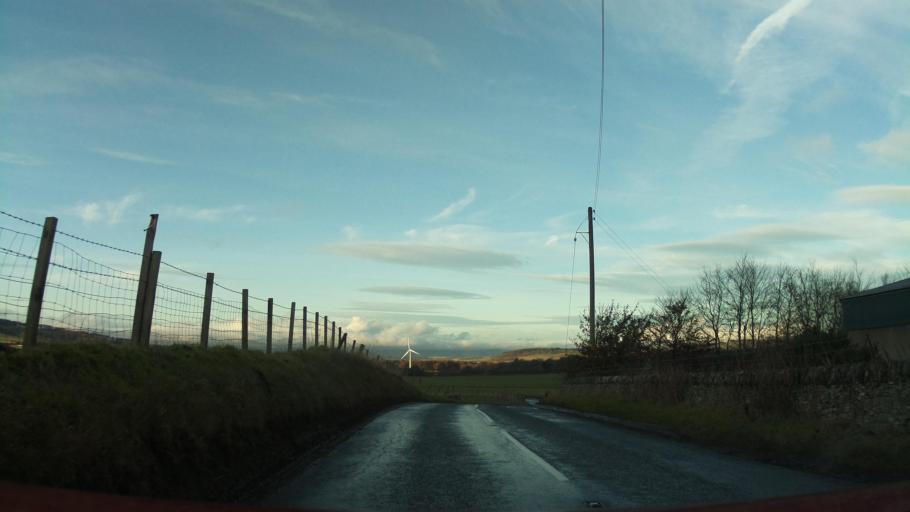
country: GB
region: Scotland
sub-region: Angus
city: Letham
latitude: 56.5810
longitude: -2.8144
